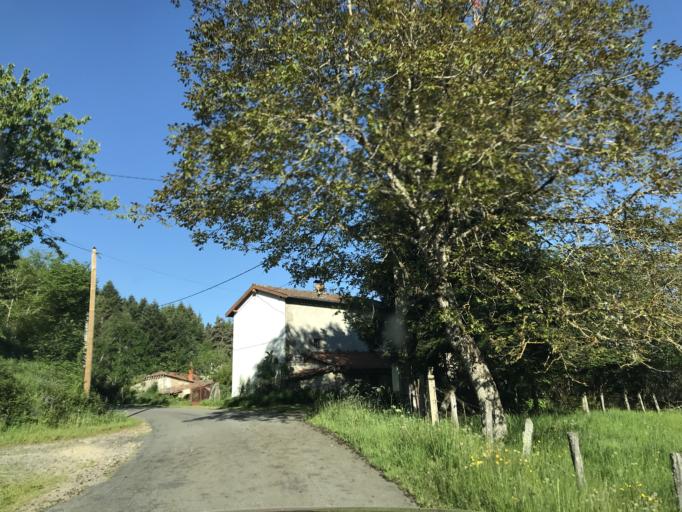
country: FR
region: Auvergne
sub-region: Departement du Puy-de-Dome
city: Job
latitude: 45.7052
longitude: 3.7024
